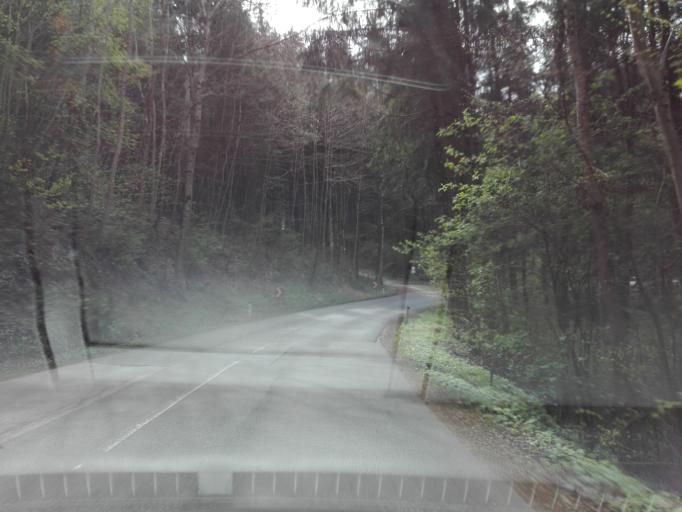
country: AT
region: Upper Austria
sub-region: Politischer Bezirk Urfahr-Umgebung
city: Gramastetten
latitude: 48.3755
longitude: 14.1896
